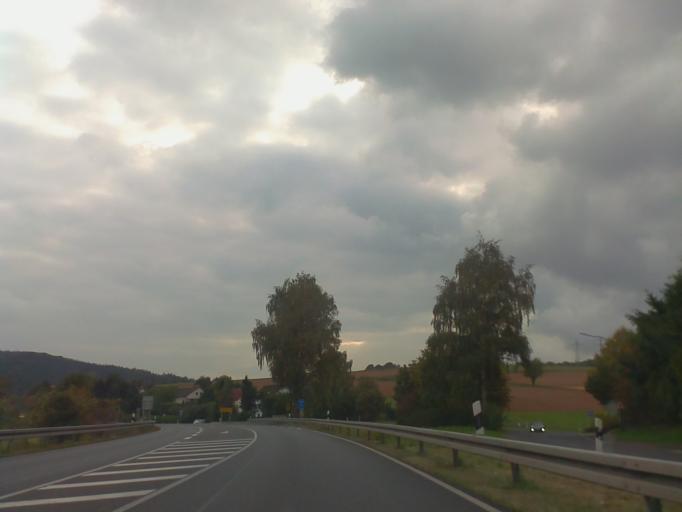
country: DE
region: Hesse
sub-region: Regierungsbezirk Kassel
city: Hunfeld
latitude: 50.6420
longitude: 9.7432
